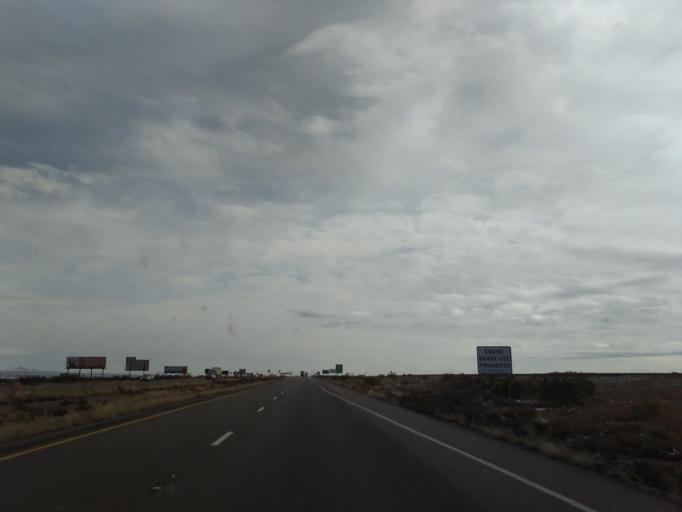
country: US
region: New Mexico
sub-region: Hidalgo County
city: Lordsburg
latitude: 32.3499
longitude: -108.7334
